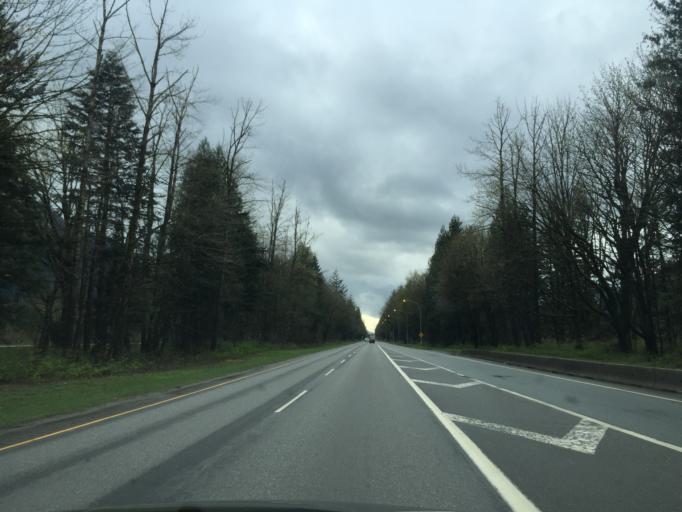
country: CA
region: British Columbia
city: Hope
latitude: 49.3449
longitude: -121.5932
